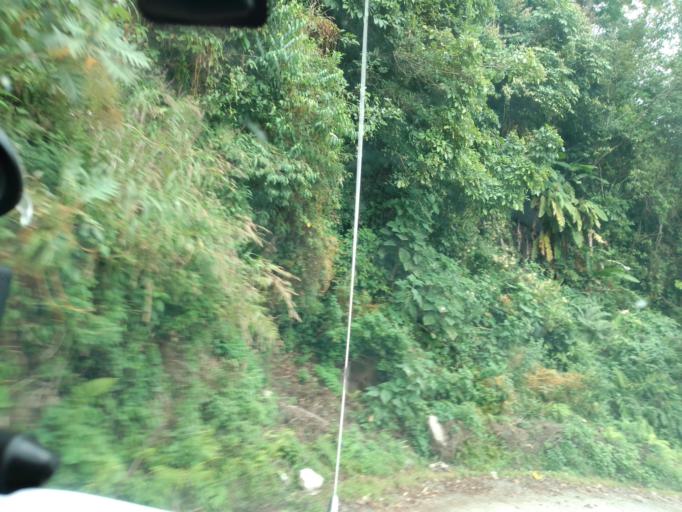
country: MX
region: Chiapas
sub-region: Union Juarez
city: Santo Domingo
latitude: 15.0942
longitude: -92.0996
